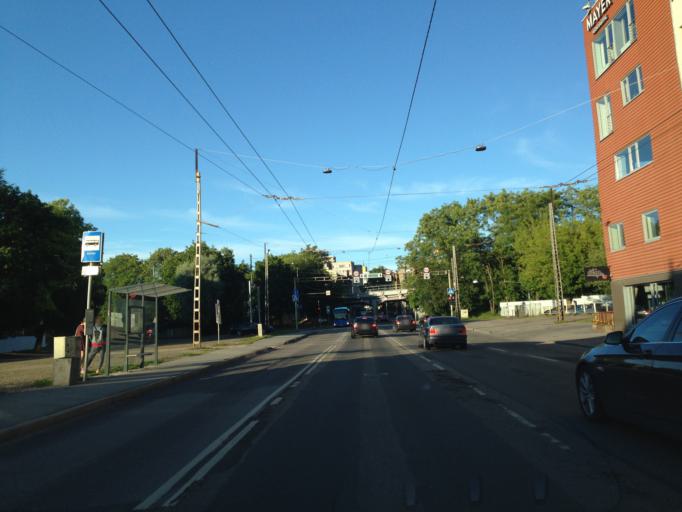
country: EE
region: Harju
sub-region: Tallinna linn
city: Tallinn
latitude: 59.4338
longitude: 24.7207
